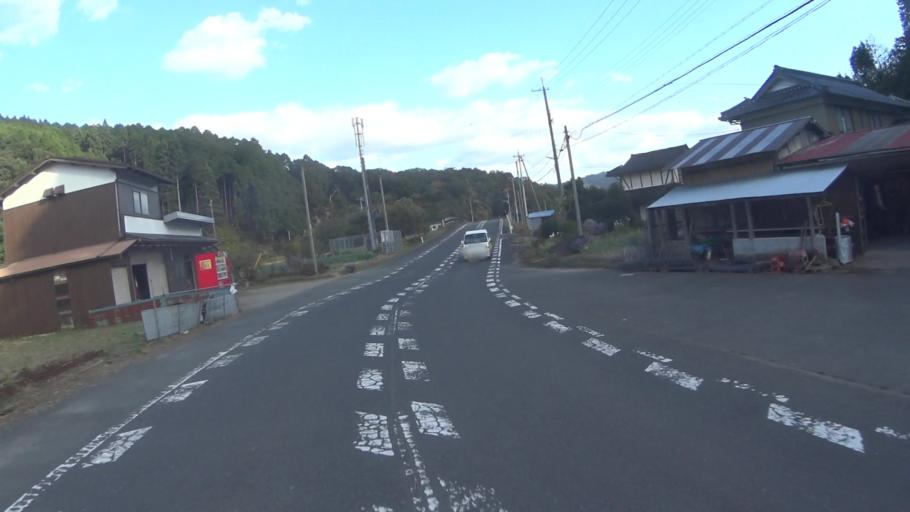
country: JP
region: Kyoto
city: Miyazu
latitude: 35.4381
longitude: 135.2210
